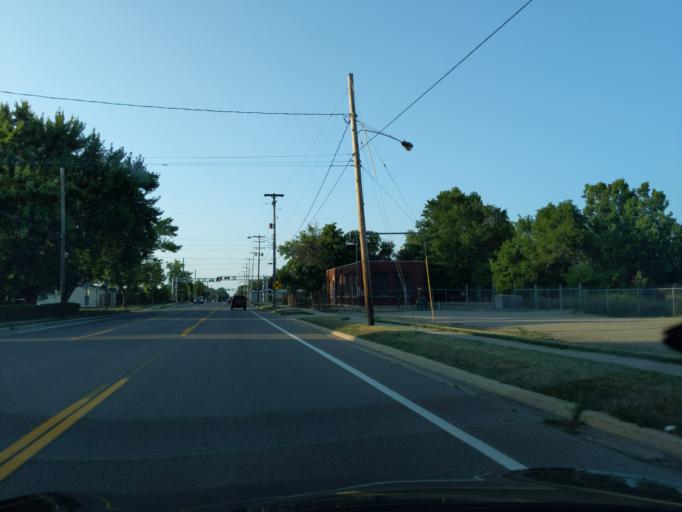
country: US
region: Michigan
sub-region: Shiawassee County
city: Owosso
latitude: 42.9920
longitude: -84.1769
